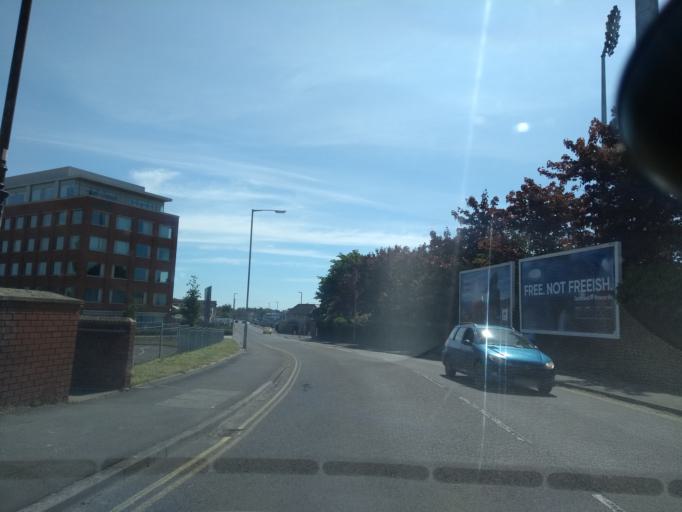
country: GB
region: England
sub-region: Somerset
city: Taunton
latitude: 51.0200
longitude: -3.1006
